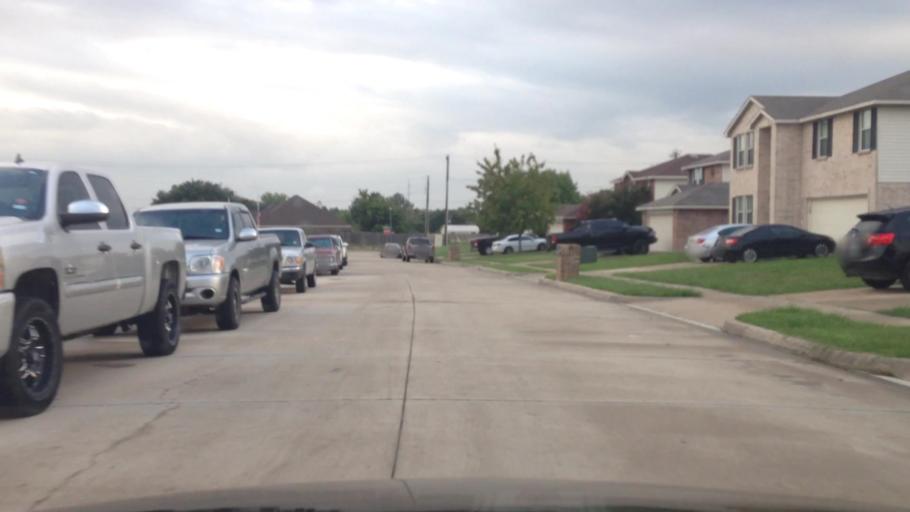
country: US
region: Texas
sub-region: Johnson County
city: Burleson
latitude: 32.5626
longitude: -97.3397
